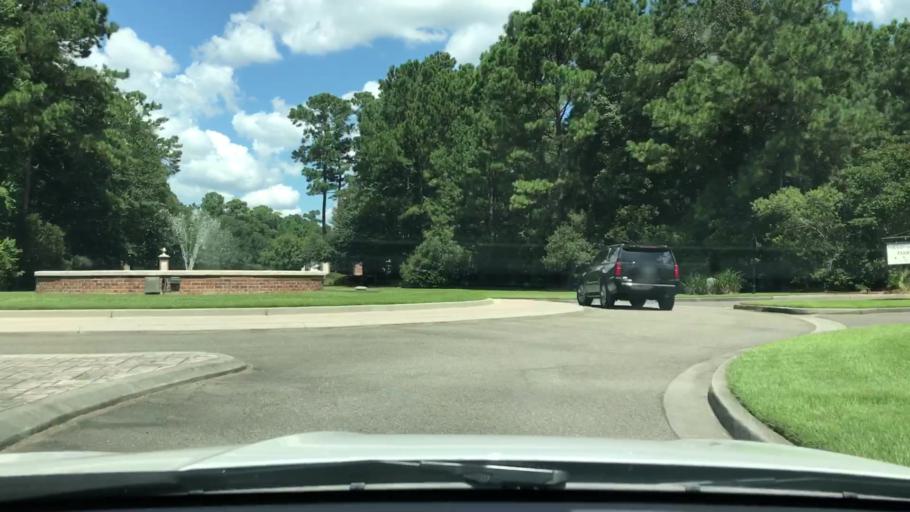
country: US
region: South Carolina
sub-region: Berkeley County
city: Hanahan
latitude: 32.9310
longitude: -79.9995
